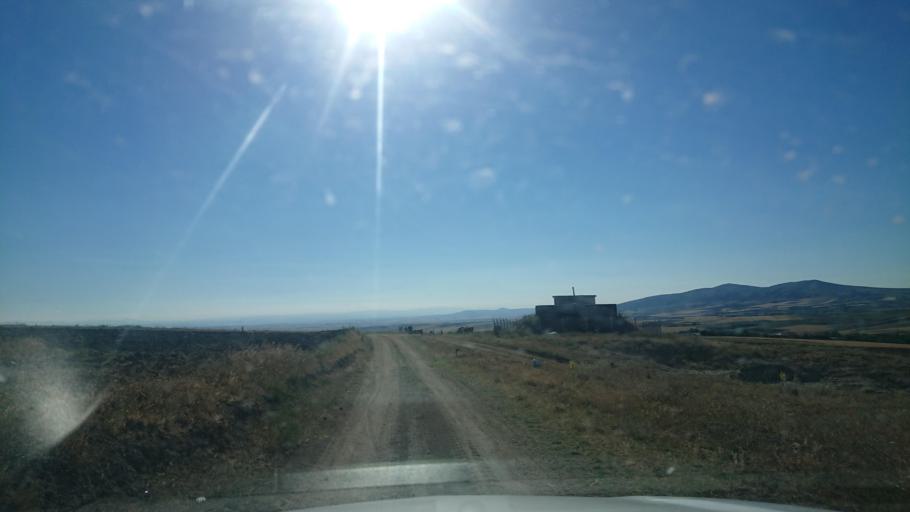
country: TR
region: Aksaray
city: Agacoren
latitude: 38.8289
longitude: 33.9469
